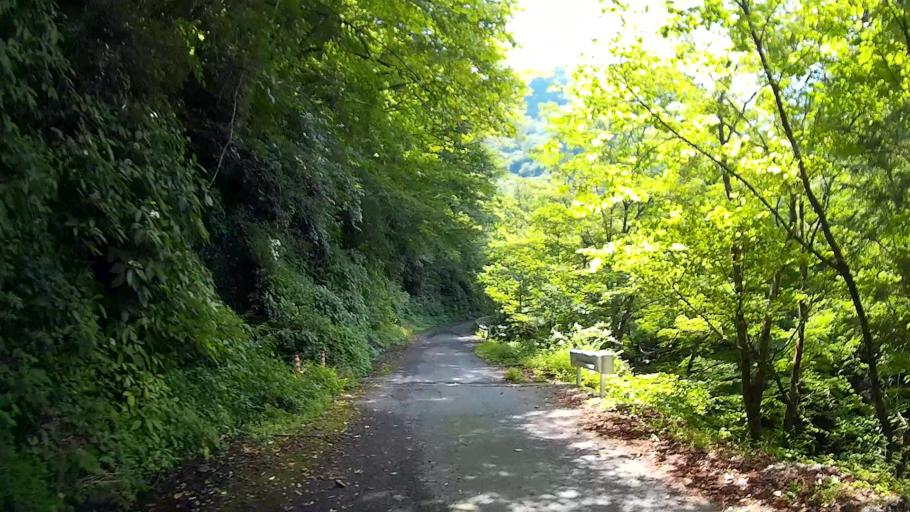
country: JP
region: Saitama
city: Chichibu
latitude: 35.8882
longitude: 139.0990
